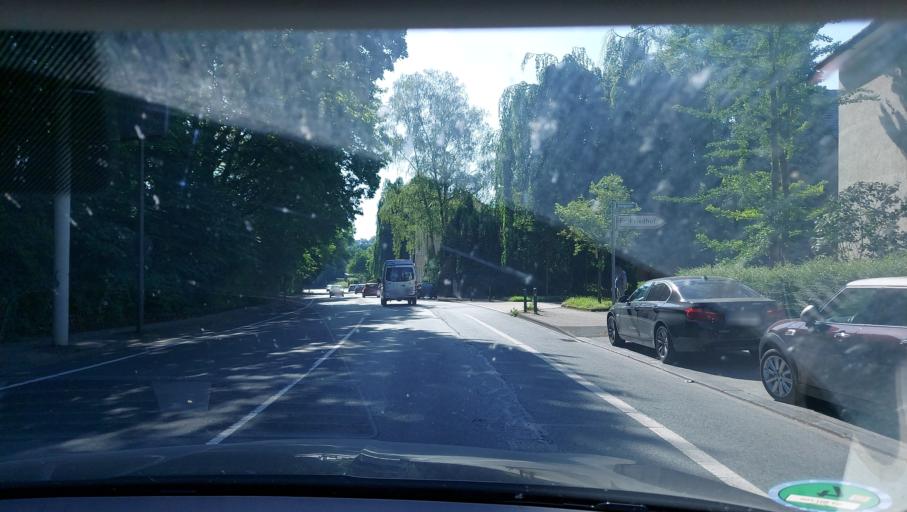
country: DE
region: North Rhine-Westphalia
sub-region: Regierungsbezirk Dusseldorf
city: Solingen
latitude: 51.1525
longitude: 7.0659
